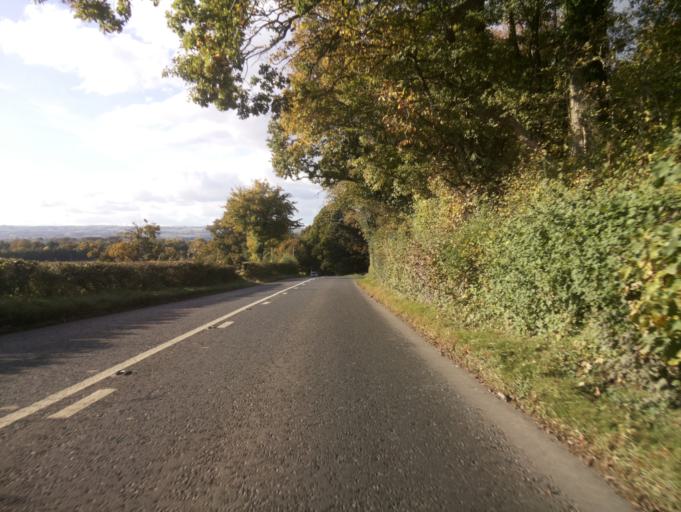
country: GB
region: England
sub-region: Herefordshire
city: Kinnersley
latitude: 52.1076
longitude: -2.9596
